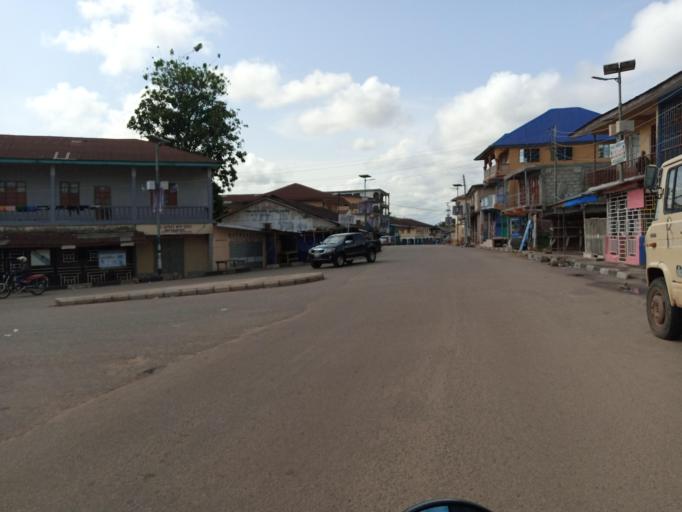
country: SL
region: Southern Province
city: Bo
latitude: 7.9656
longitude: -11.7405
